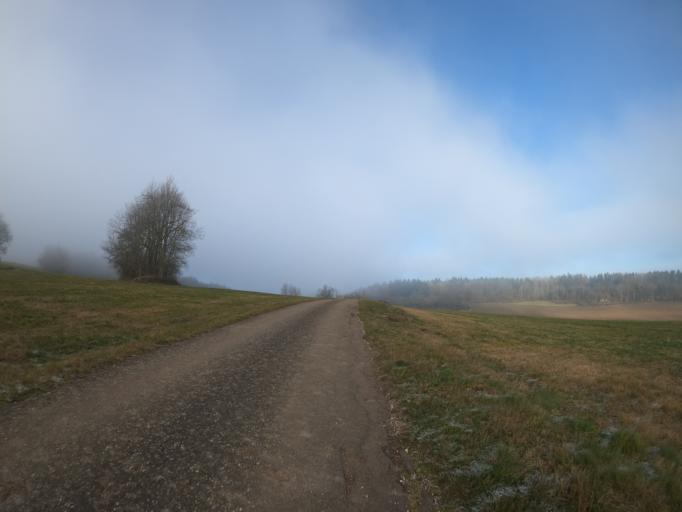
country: DE
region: Baden-Wuerttemberg
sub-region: Regierungsbezirk Stuttgart
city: Deggingen
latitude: 48.5916
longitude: 9.7517
